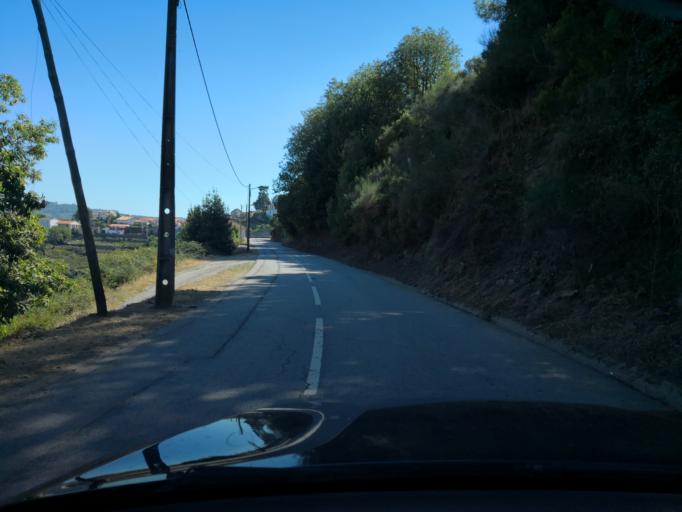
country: PT
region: Vila Real
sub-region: Santa Marta de Penaguiao
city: Santa Marta de Penaguiao
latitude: 41.2307
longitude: -7.7934
